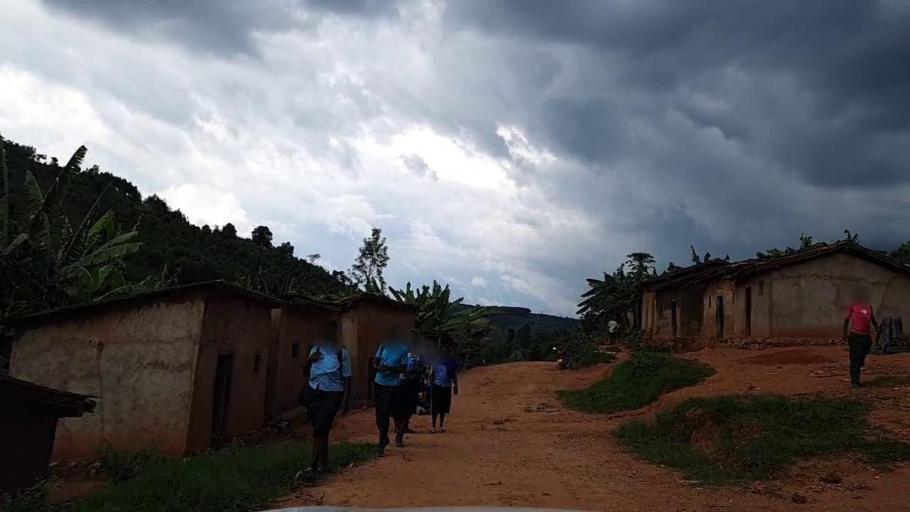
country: RW
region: Southern Province
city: Nyanza
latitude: -2.3923
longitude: 29.6881
